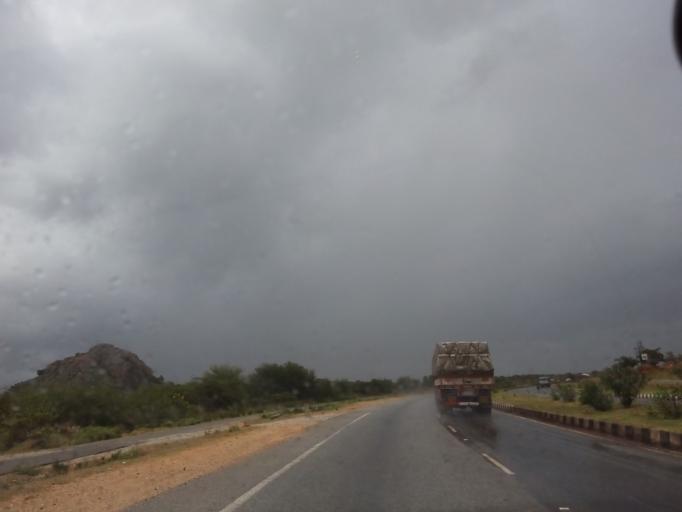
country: IN
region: Karnataka
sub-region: Chitradurga
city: Chitradurga
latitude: 14.2580
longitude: 76.3599
